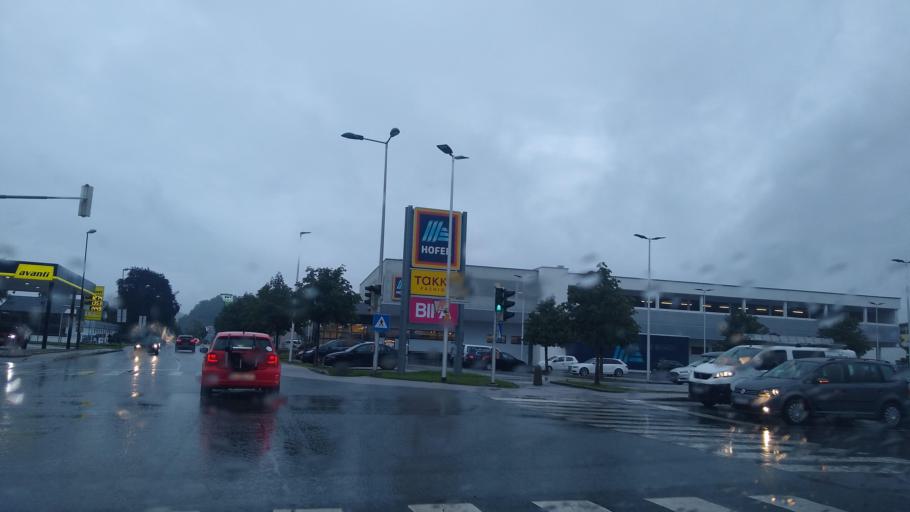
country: AT
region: Tyrol
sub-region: Politischer Bezirk Kufstein
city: Worgl
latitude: 47.4889
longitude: 12.0732
